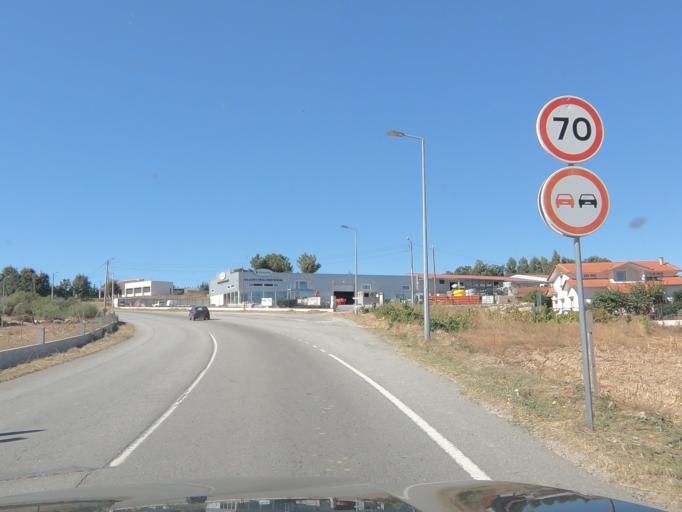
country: PT
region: Vila Real
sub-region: Valpacos
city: Valpacos
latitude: 41.6709
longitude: -7.3387
